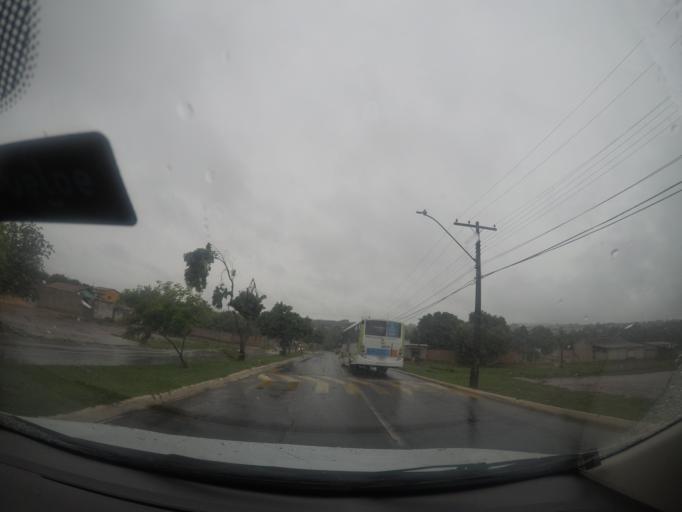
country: BR
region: Goias
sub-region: Goiania
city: Goiania
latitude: -16.6112
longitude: -49.3373
